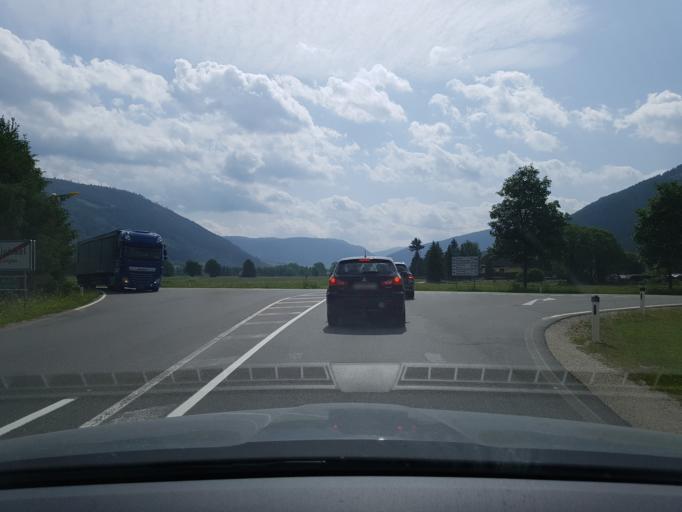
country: AT
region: Salzburg
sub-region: Politischer Bezirk Tamsweg
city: Sankt Michael im Lungau
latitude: 47.0951
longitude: 13.6401
